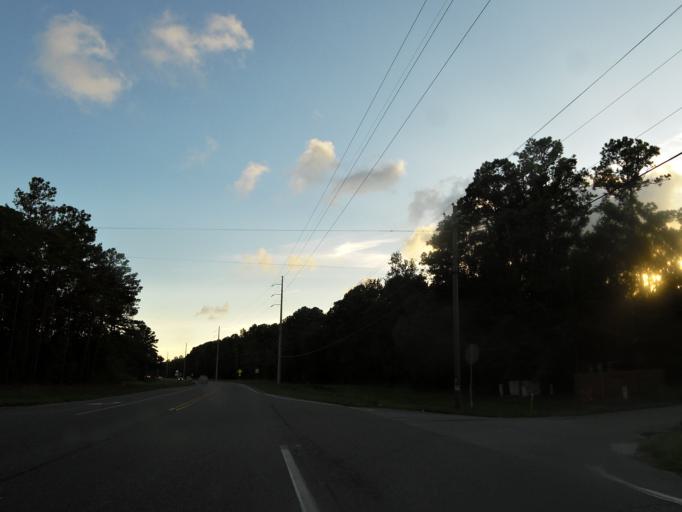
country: US
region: Georgia
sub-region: Glynn County
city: Dock Junction
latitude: 31.1362
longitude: -81.5960
